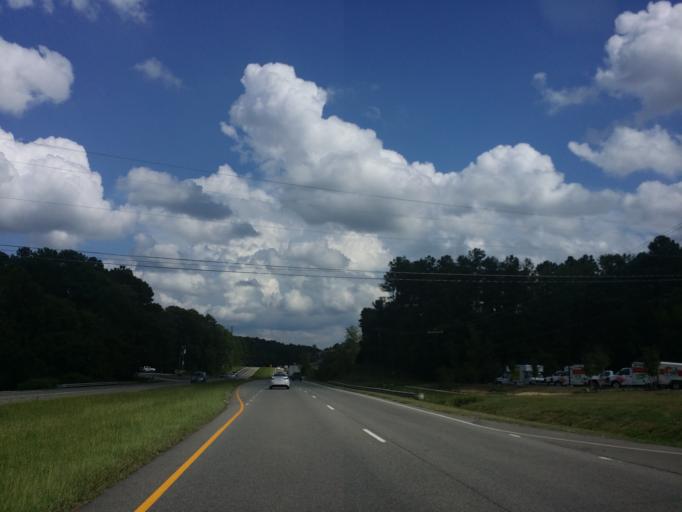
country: US
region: North Carolina
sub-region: Durham County
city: Durham
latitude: 35.9414
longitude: -78.8234
